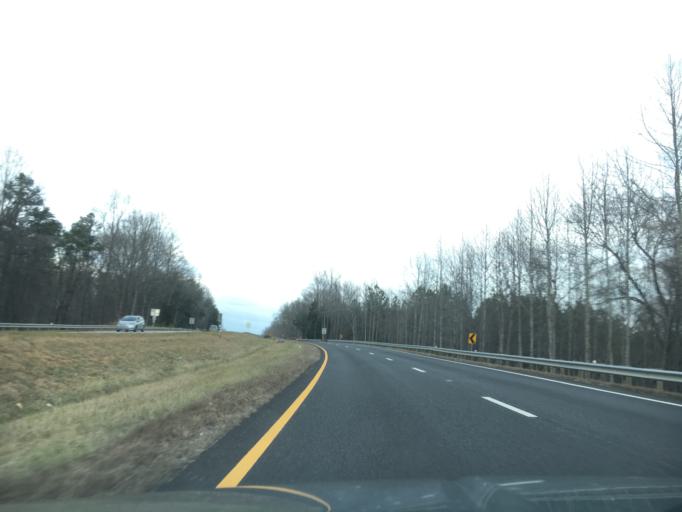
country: US
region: Virginia
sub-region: Prince Edward County
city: Hampden Sydney
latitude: 37.1060
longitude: -78.3573
